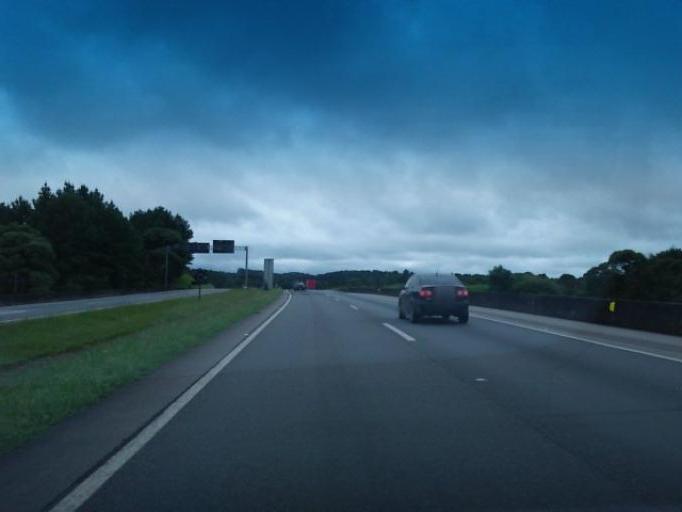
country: BR
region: Parana
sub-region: Quatro Barras
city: Quatro Barras
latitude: -25.3521
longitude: -49.0421
